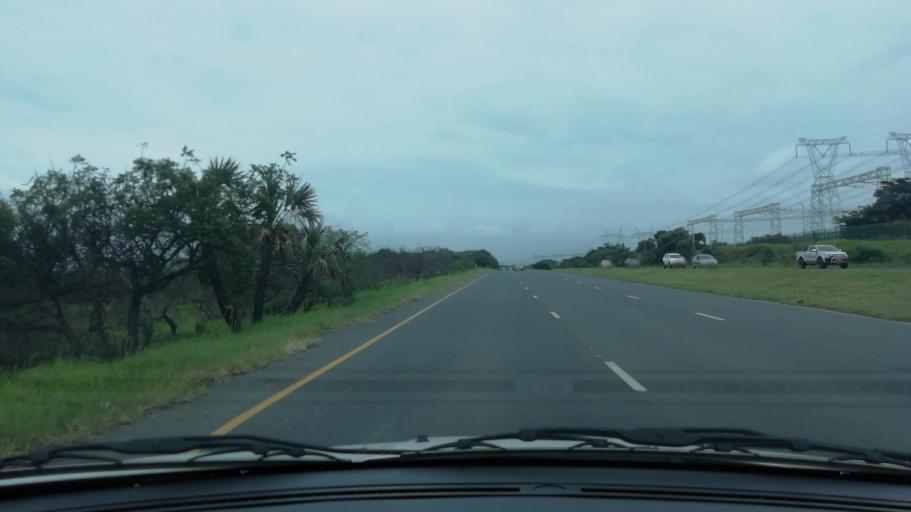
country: ZA
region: KwaZulu-Natal
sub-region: uThungulu District Municipality
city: Richards Bay
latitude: -28.7723
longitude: 32.0226
